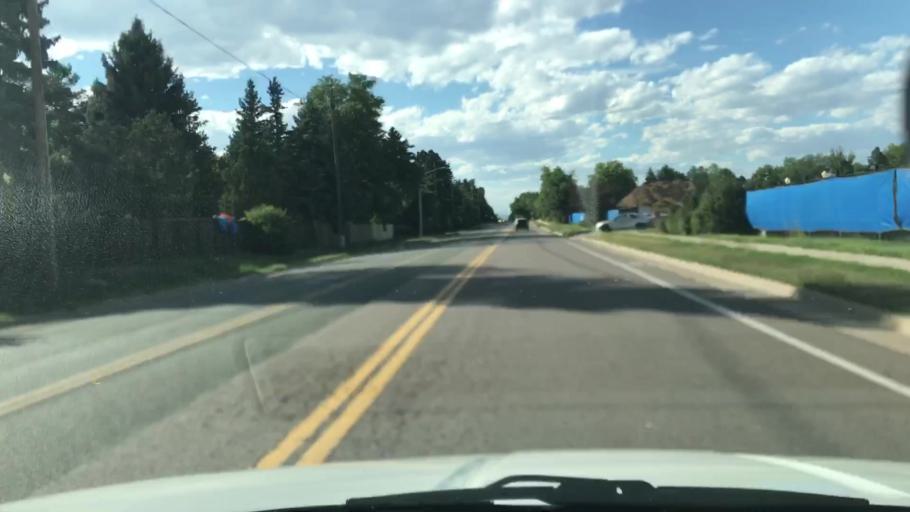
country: US
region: Colorado
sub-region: Arapahoe County
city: Greenwood Village
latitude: 39.6405
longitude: -104.9156
